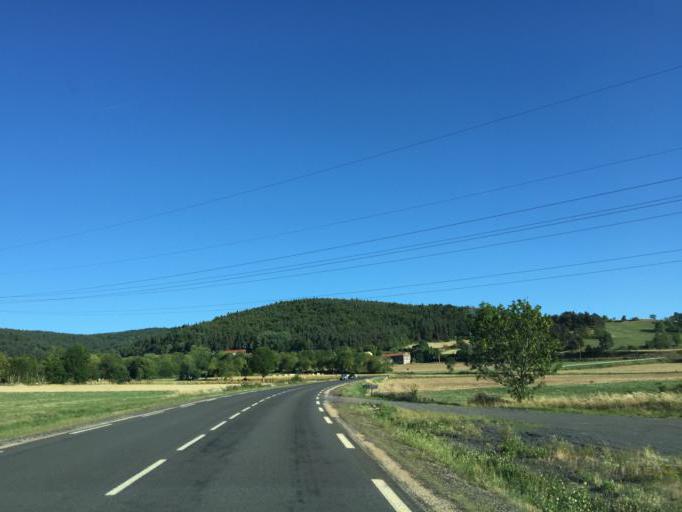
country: FR
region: Auvergne
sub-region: Departement de la Haute-Loire
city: Bains
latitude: 45.0013
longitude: 3.6891
